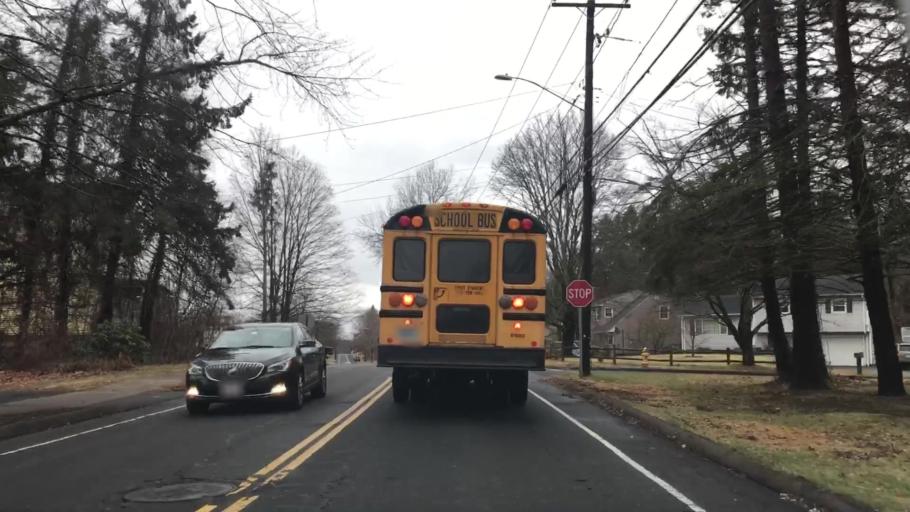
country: US
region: Connecticut
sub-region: Tolland County
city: Rockville
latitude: 41.8637
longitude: -72.4932
